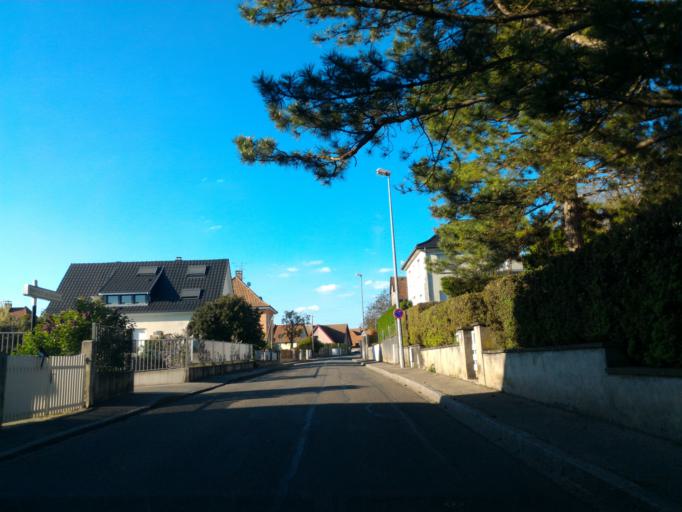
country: FR
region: Alsace
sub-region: Departement du Haut-Rhin
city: Riedisheim
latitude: 47.7491
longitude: 7.3717
